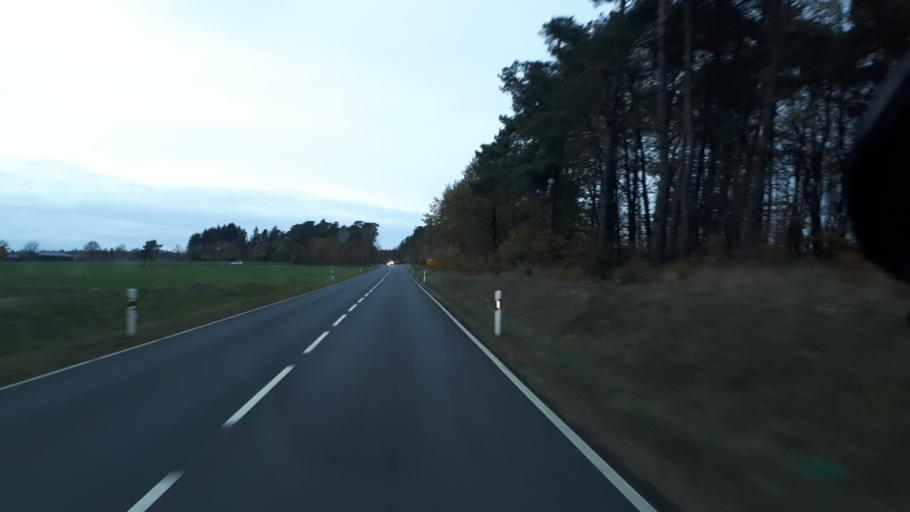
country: DE
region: Rheinland-Pfalz
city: Alflen
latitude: 50.1865
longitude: 7.0417
